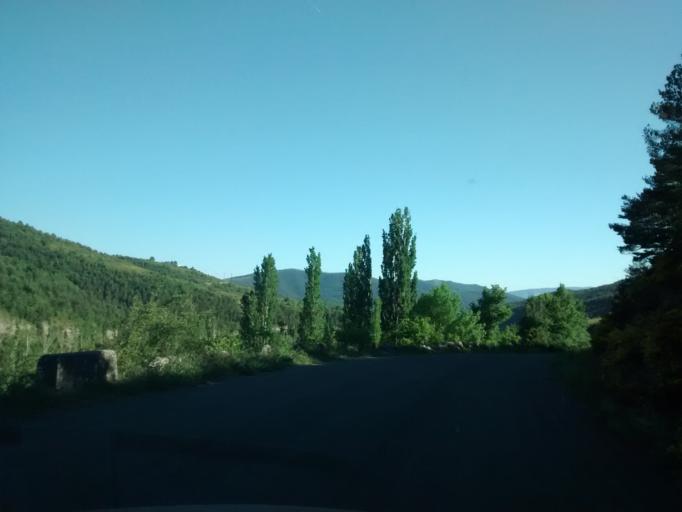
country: ES
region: Aragon
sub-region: Provincia de Huesca
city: Jasa
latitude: 42.6950
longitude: -0.6202
